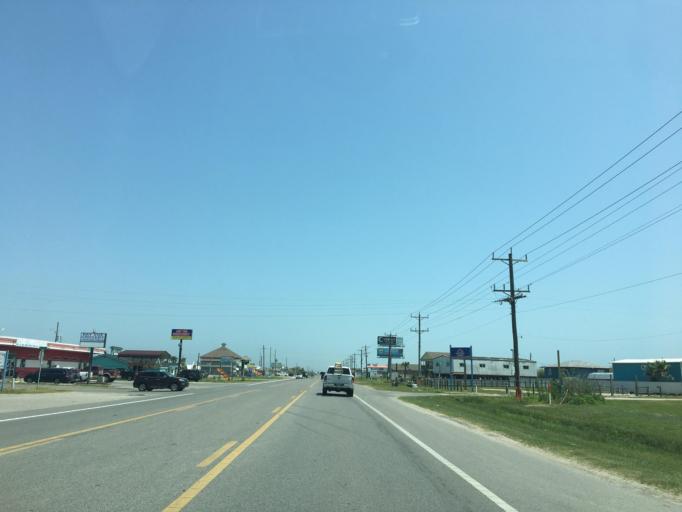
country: US
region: Texas
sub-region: Galveston County
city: Bolivar Peninsula
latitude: 29.4584
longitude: -94.6370
